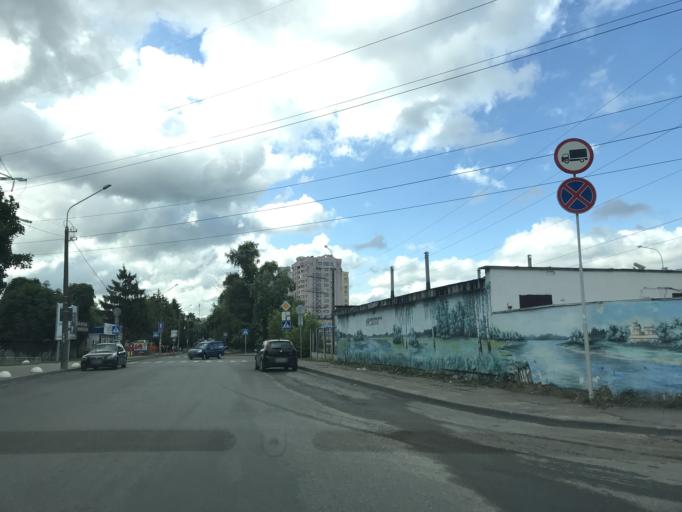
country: BY
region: Minsk
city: Borovlyany
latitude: 53.9554
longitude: 27.6906
